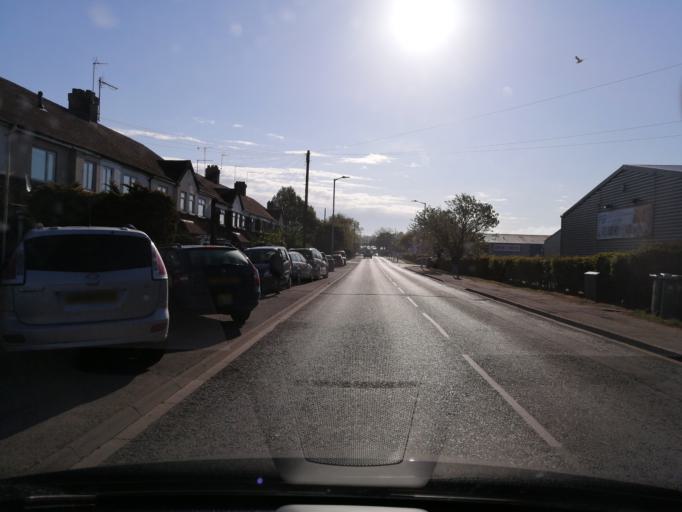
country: GB
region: England
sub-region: Peterborough
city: Peterborough
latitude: 52.5709
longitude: -0.2214
